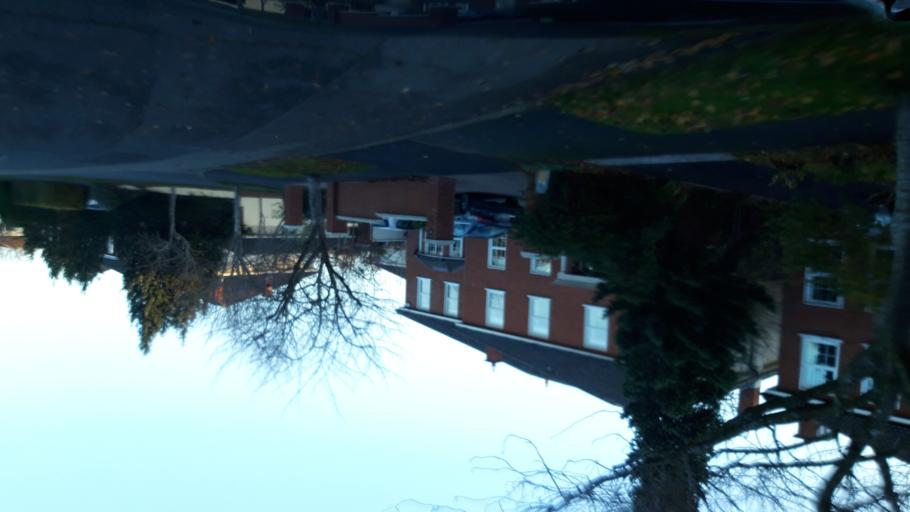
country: IE
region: Leinster
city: Castleknock
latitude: 53.3679
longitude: -6.3563
